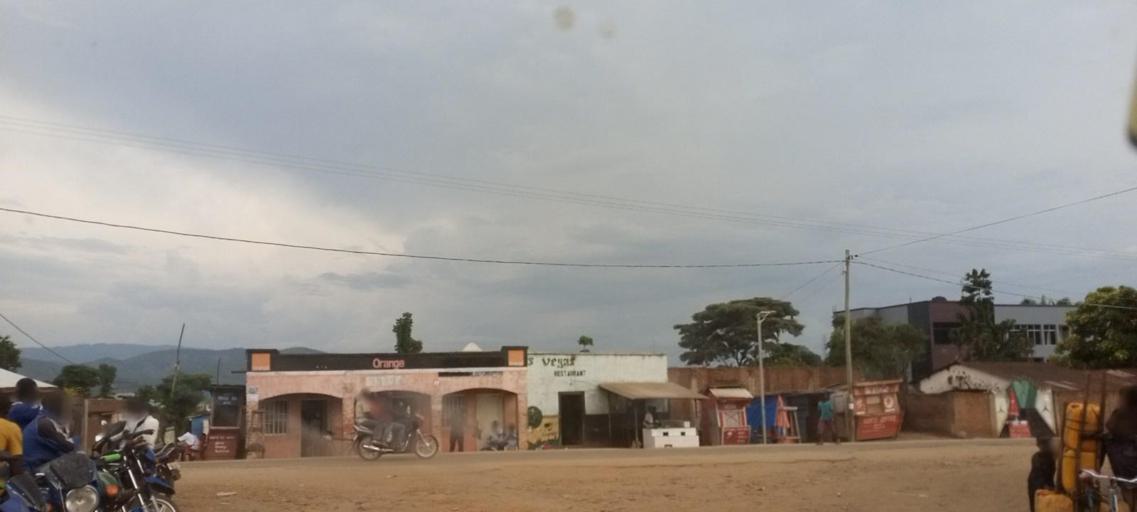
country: BI
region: Cibitoke
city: Cibitoke
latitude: -2.7323
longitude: 29.0034
